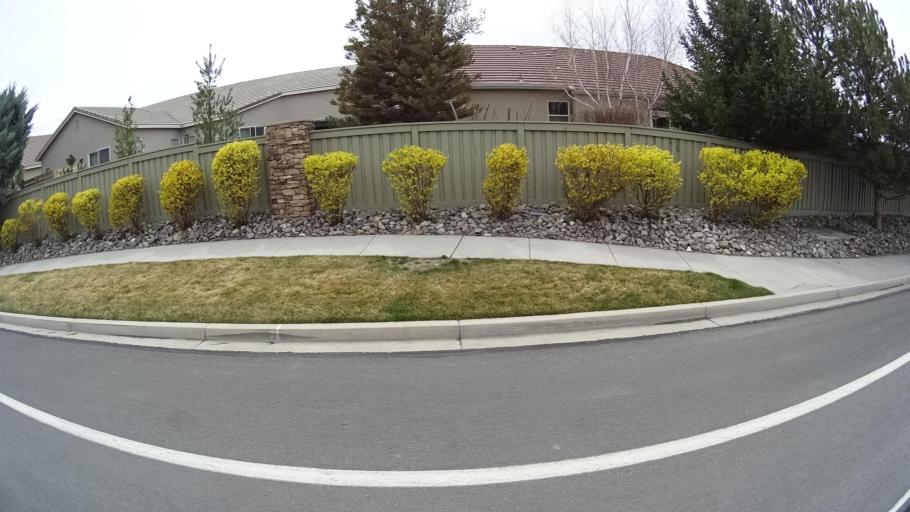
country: US
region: Nevada
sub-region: Washoe County
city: Sparks
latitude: 39.4353
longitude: -119.7374
